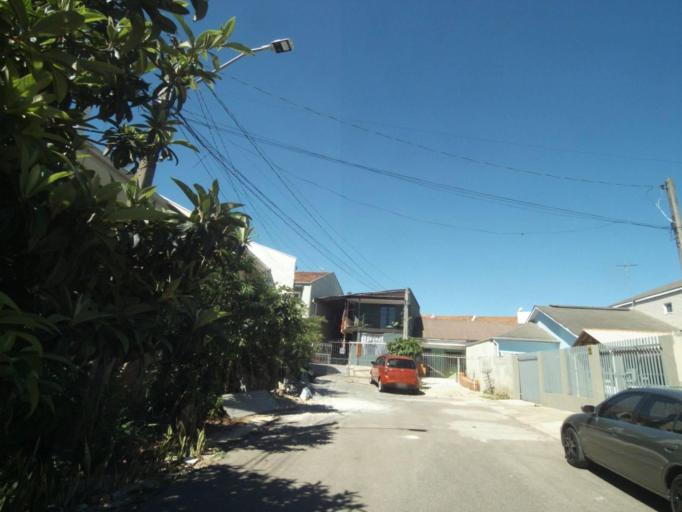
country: BR
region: Parana
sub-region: Curitiba
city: Curitiba
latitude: -25.4610
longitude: -49.3495
